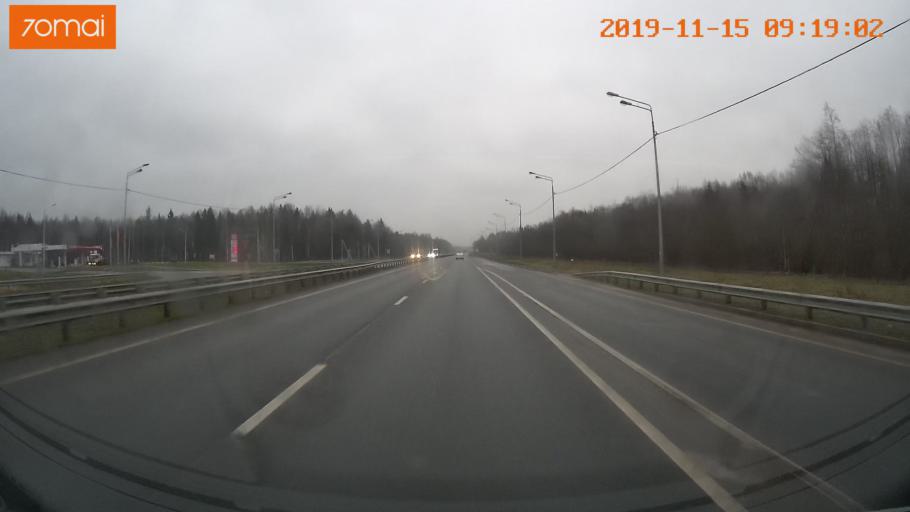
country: RU
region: Vologda
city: Tonshalovo
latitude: 59.2803
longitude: 38.0081
